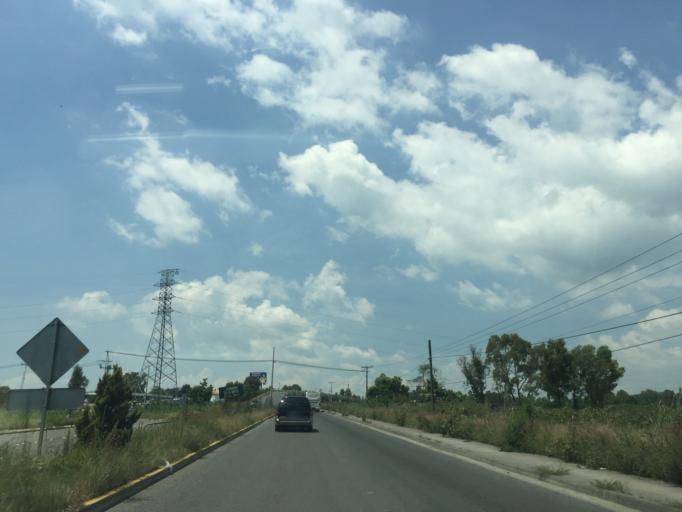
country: MX
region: Guanajuato
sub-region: Leon
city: Fraccionamiento Paseo de las Torres
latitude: 21.1754
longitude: -101.7382
